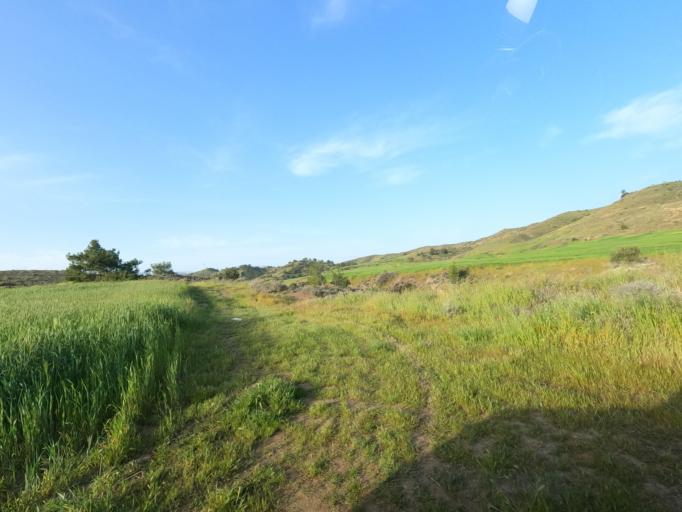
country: CY
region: Lefkosia
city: Lefka
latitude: 35.0855
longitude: 32.9434
